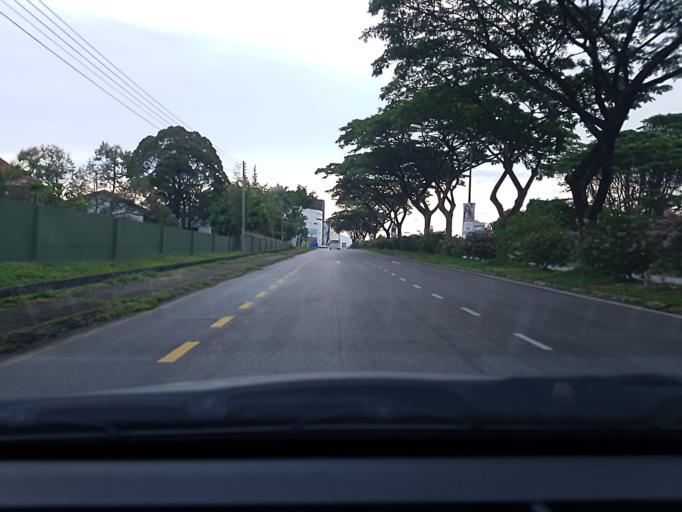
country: MY
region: Sarawak
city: Kuching
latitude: 1.5193
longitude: 110.3590
